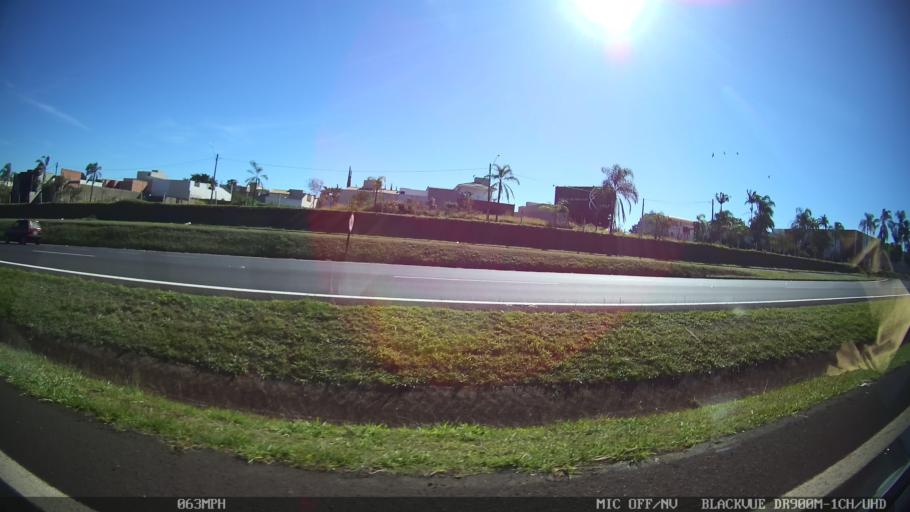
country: BR
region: Sao Paulo
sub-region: Franca
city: Franca
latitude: -20.5702
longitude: -47.3957
